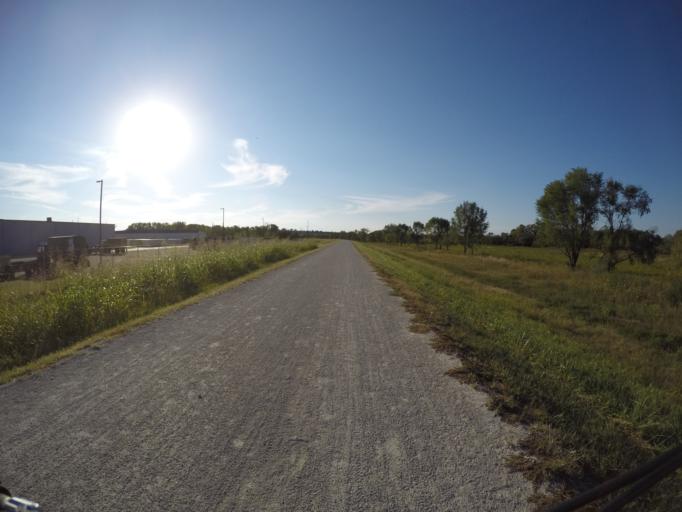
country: US
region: Kansas
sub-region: Riley County
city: Manhattan
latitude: 39.1961
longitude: -96.5418
